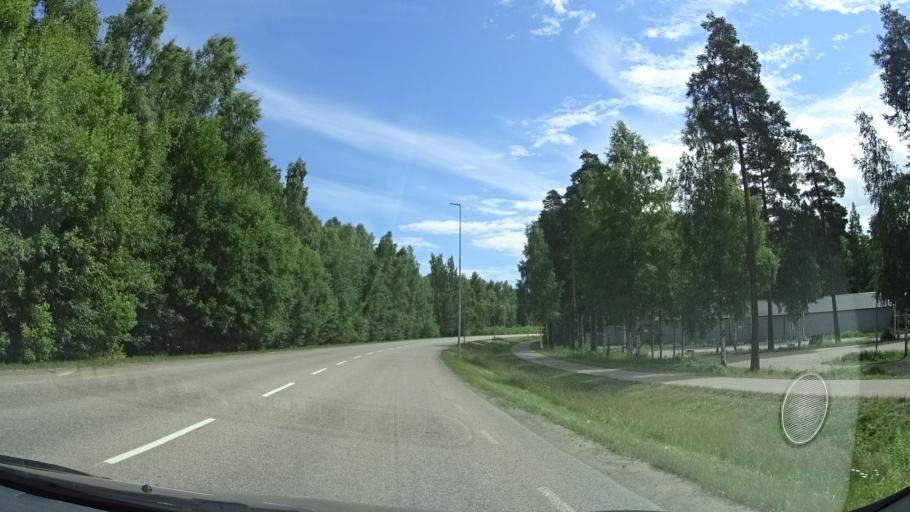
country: SE
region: Vaestmanland
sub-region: Vasteras
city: Hokasen
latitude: 59.6430
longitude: 16.5844
